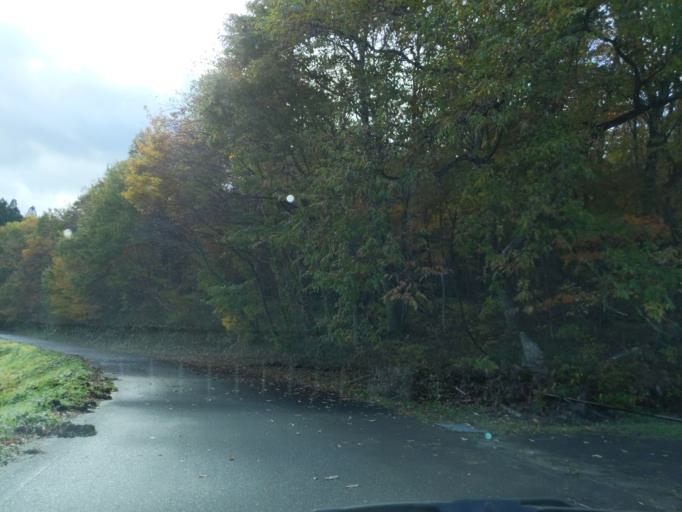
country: JP
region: Iwate
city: Ichinoseki
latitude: 38.9789
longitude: 140.9473
